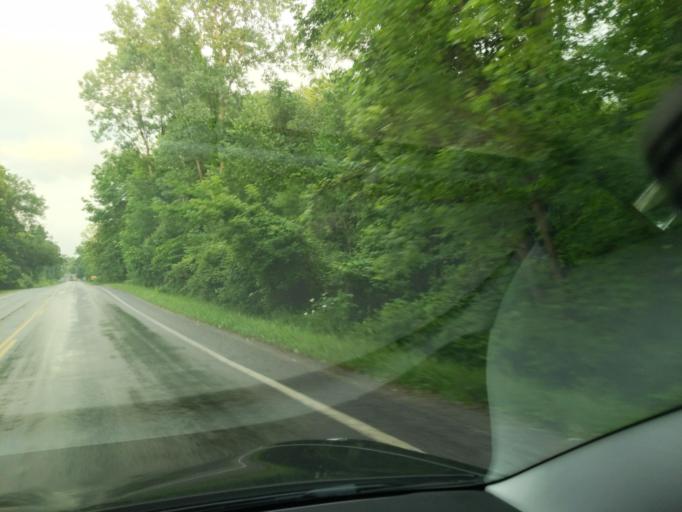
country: US
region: Michigan
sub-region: Ingham County
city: Mason
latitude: 42.5237
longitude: -84.3613
